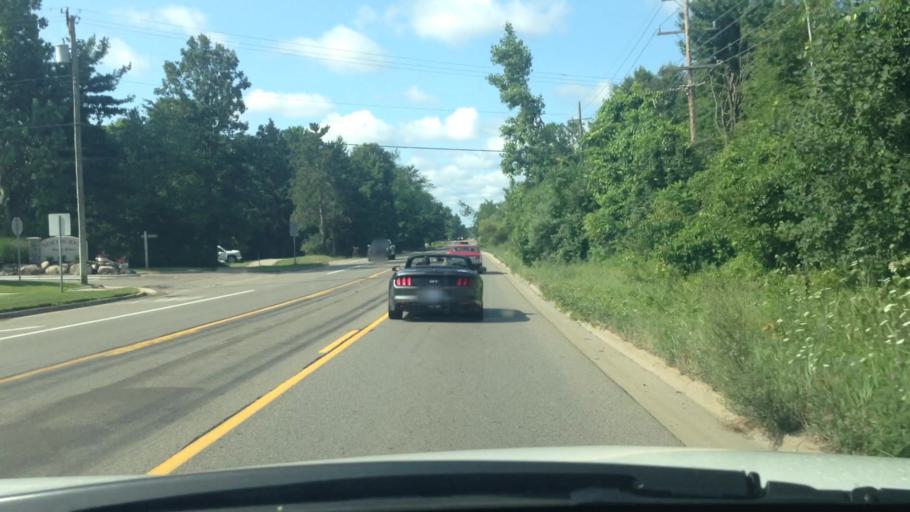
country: US
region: Michigan
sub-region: Oakland County
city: Clarkston
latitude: 42.7235
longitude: -83.4308
